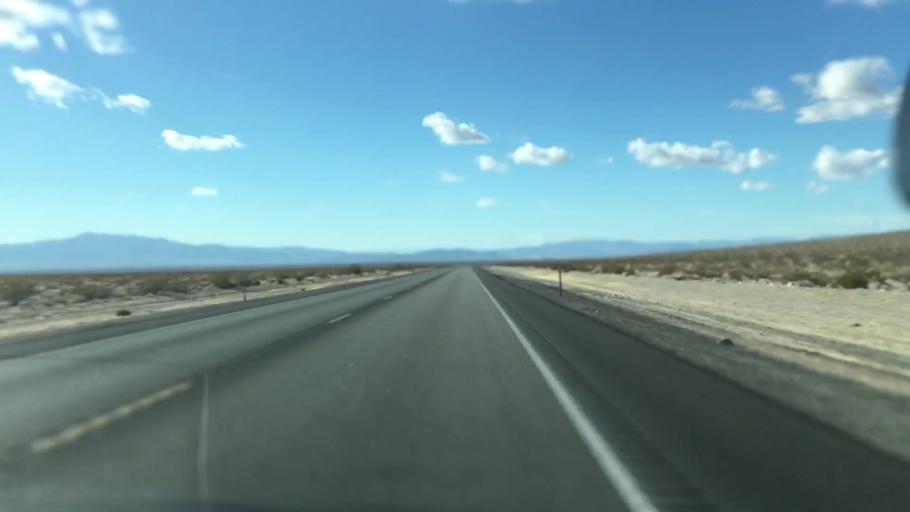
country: US
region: Nevada
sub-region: Nye County
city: Beatty
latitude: 36.6318
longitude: -116.3340
